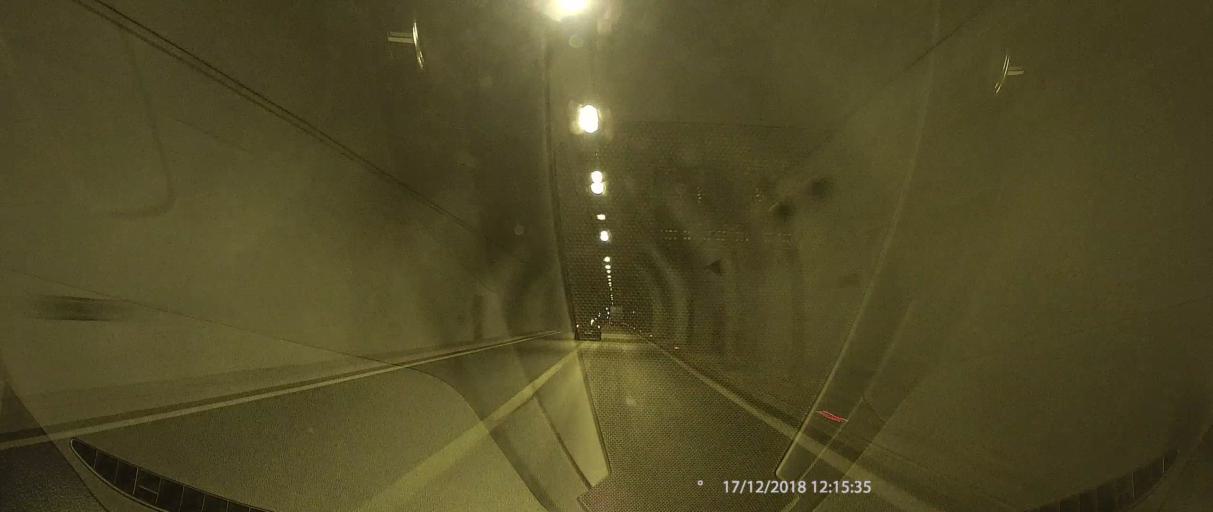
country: GR
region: Epirus
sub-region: Nomos Ioanninon
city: Metsovo
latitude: 39.7199
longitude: 21.0235
